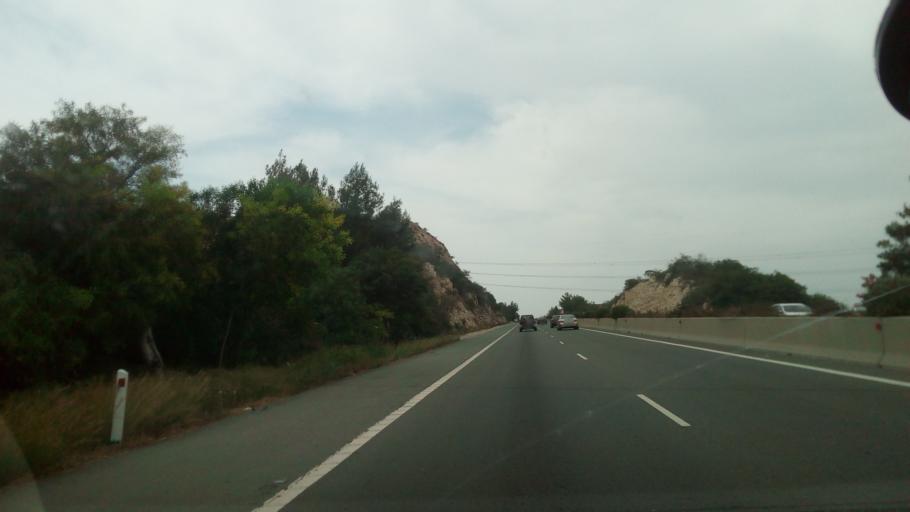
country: CY
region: Lefkosia
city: Lympia
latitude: 34.9873
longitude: 33.5060
